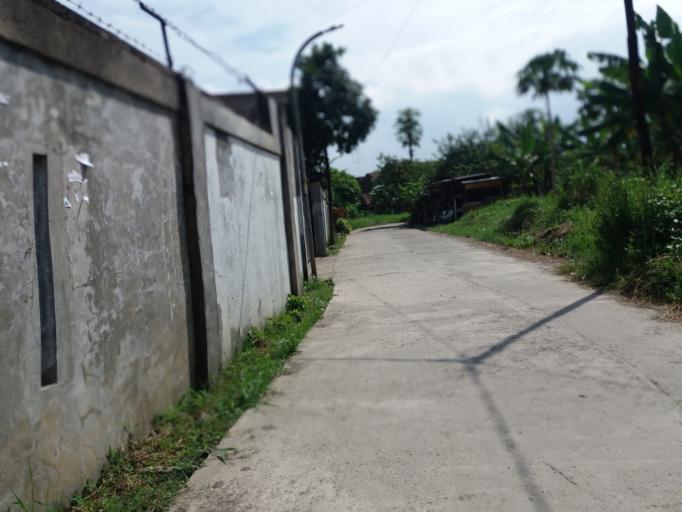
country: ID
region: West Java
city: Bandung
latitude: -6.9200
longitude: 107.6645
